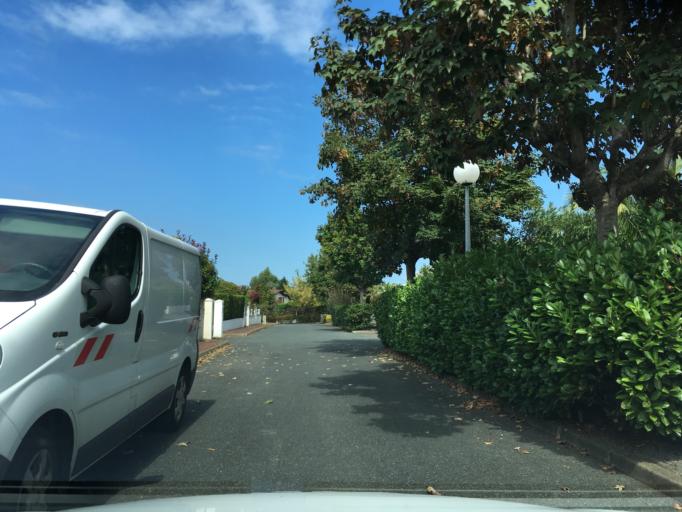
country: FR
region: Aquitaine
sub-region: Departement des Pyrenees-Atlantiques
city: Mouguerre
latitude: 43.4948
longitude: -1.4355
